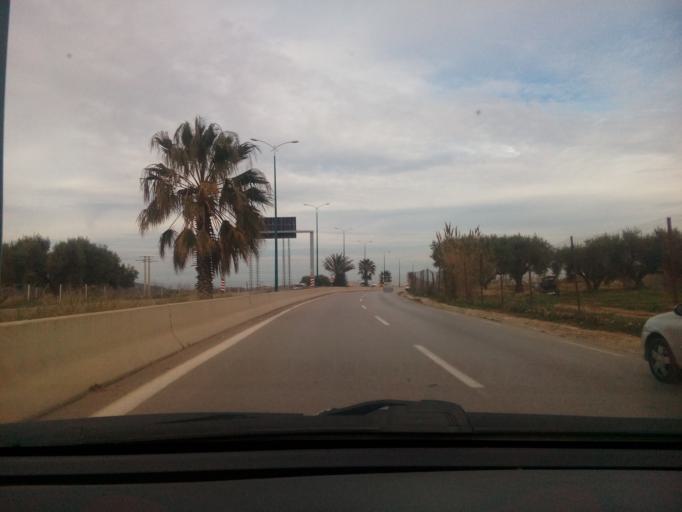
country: DZ
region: Tlemcen
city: Mansoura
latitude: 34.8683
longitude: -1.3496
